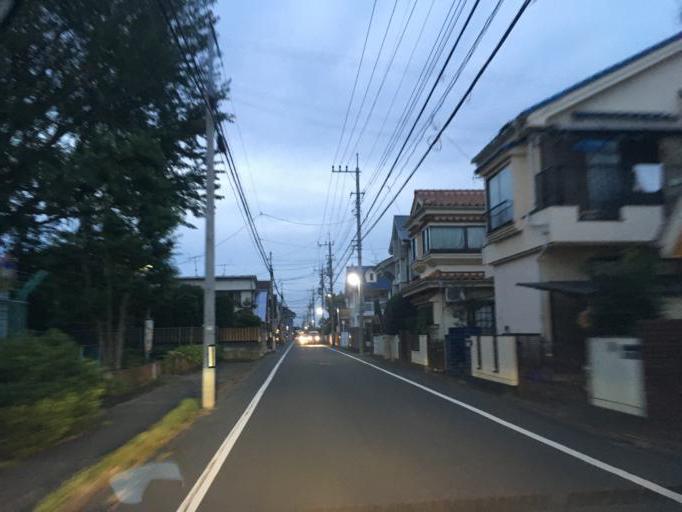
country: JP
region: Tokyo
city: Kokubunji
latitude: 35.7265
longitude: 139.4577
